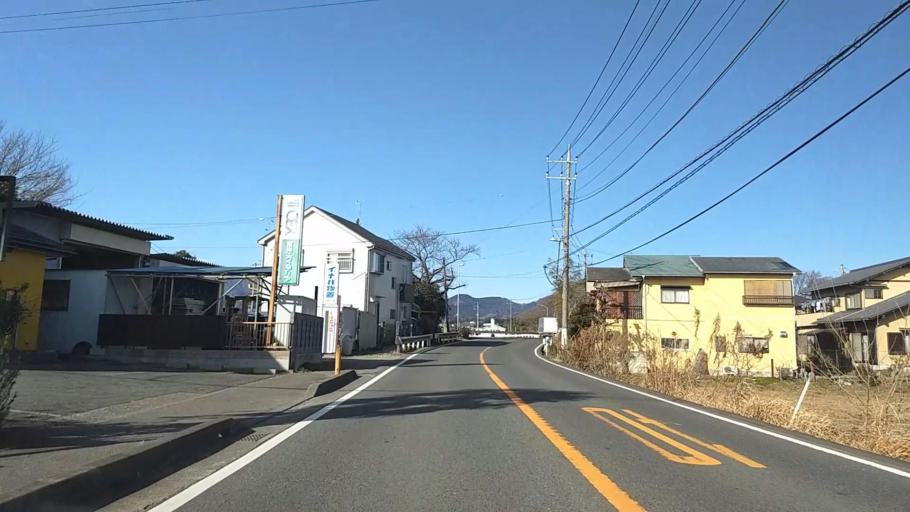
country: JP
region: Kanagawa
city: Atsugi
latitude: 35.4646
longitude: 139.3433
